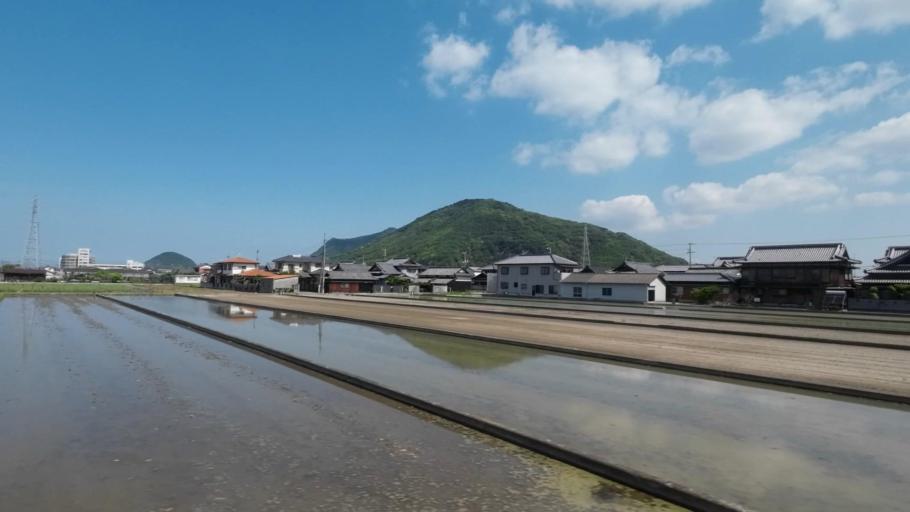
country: JP
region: Kagawa
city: Kan'onjicho
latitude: 34.1300
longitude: 133.6739
